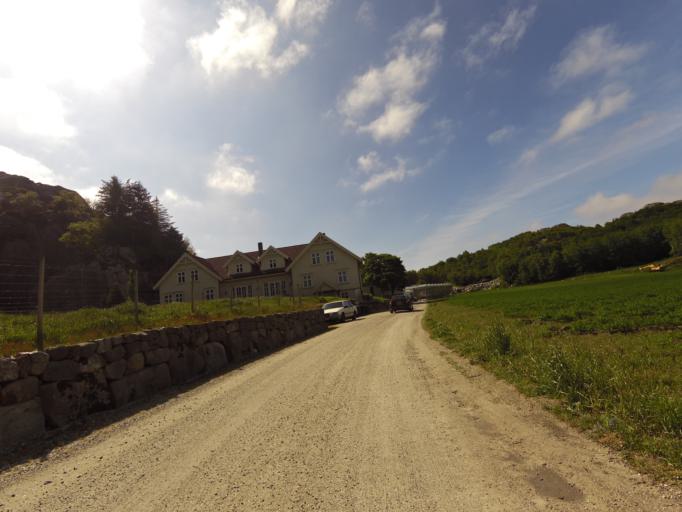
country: NO
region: Rogaland
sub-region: Ha
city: Vigrestad
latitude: 58.5161
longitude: 5.8228
